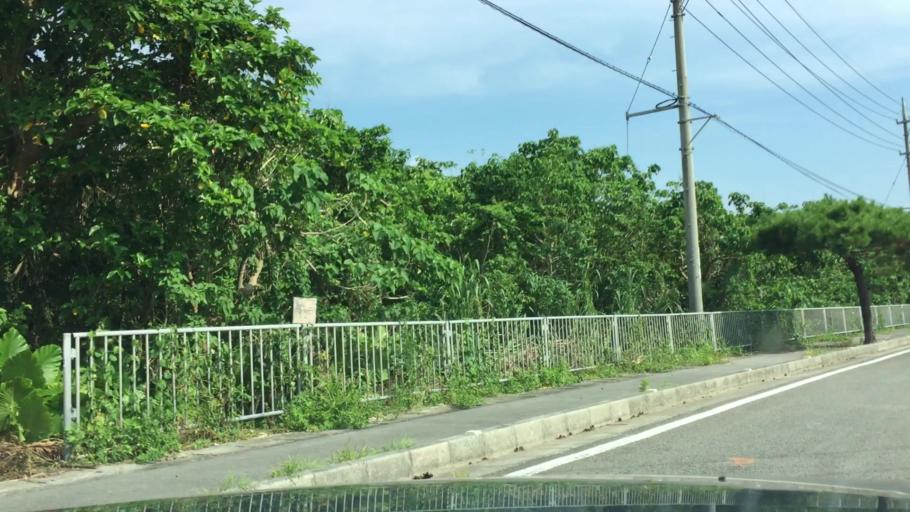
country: JP
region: Okinawa
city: Ishigaki
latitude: 24.4950
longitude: 124.2798
